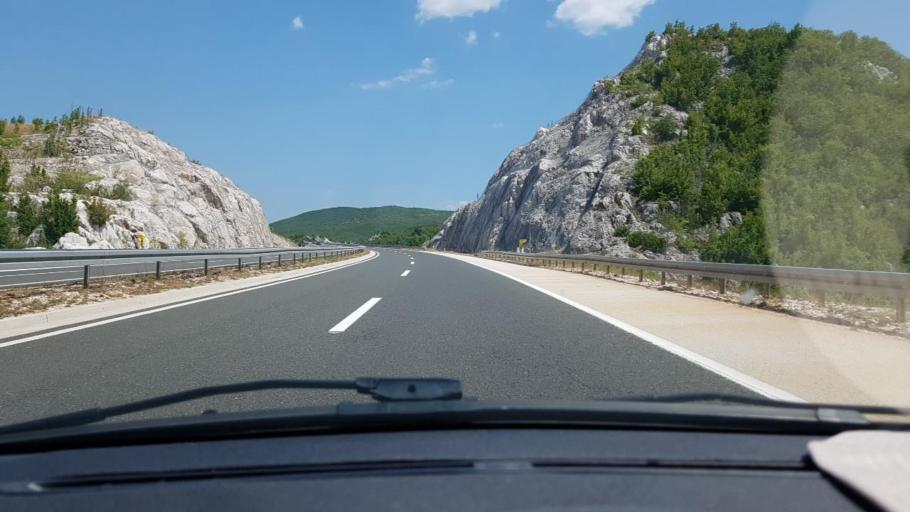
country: HR
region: Splitsko-Dalmatinska
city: Grubine
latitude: 43.3511
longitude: 17.1172
